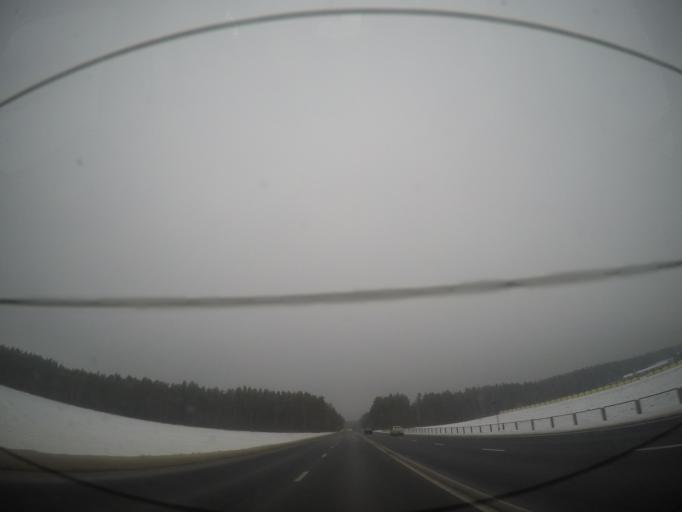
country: BY
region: Grodnenskaya
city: Hrodna
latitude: 53.6228
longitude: 23.8768
